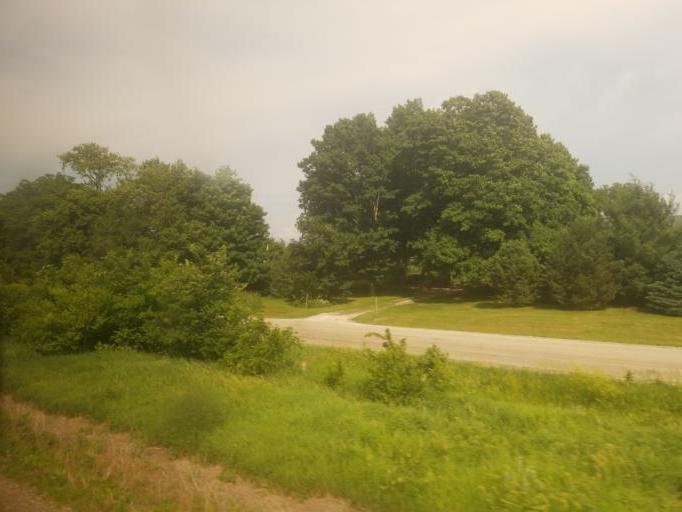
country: US
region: Illinois
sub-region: Knox County
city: Galesburg
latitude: 41.0170
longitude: -90.2902
